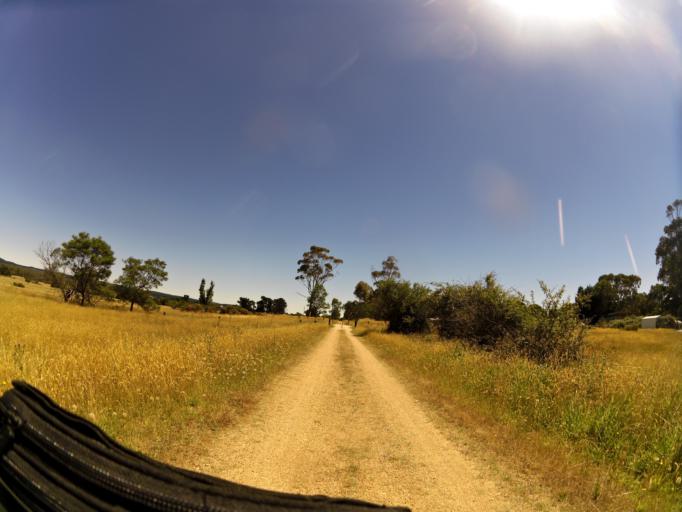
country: AU
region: Victoria
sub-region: Ballarat North
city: Delacombe
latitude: -37.6935
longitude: 143.6546
